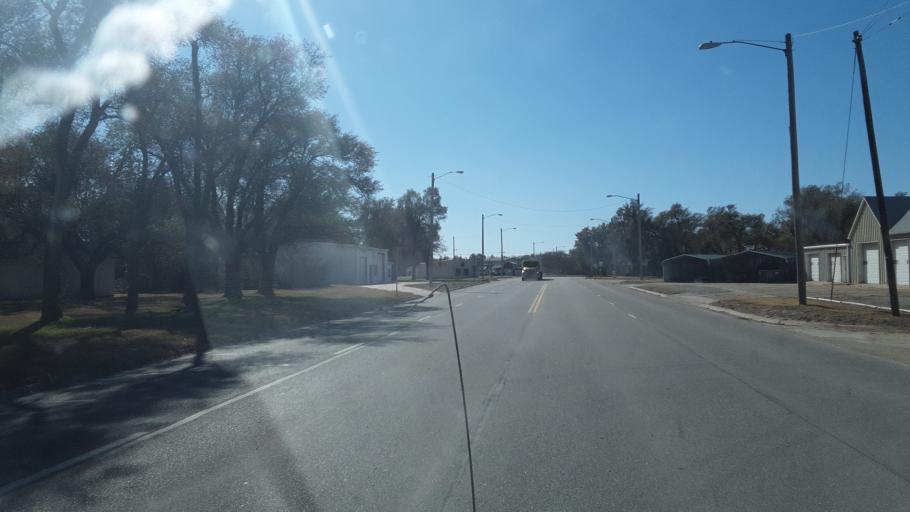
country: US
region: Kansas
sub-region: Rice County
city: Lyons
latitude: 38.3496
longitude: -98.1885
